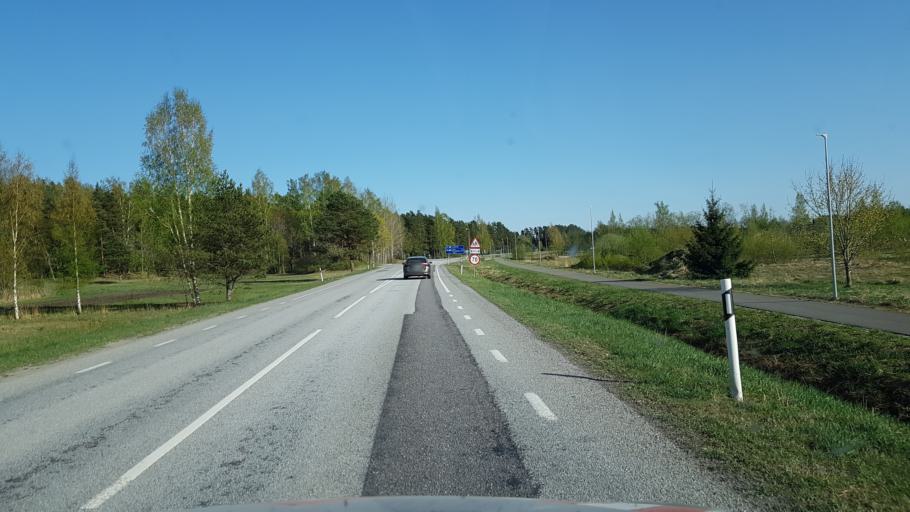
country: EE
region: Paernumaa
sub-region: Paikuse vald
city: Paikuse
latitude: 58.3593
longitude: 24.6563
